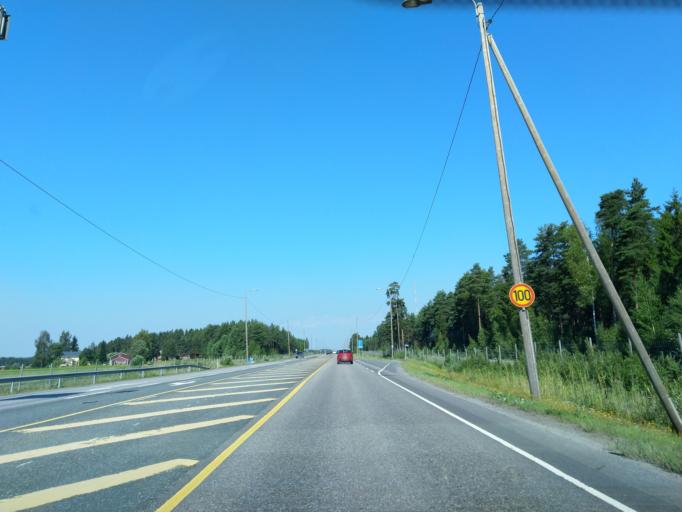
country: FI
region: Satakunta
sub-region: Pori
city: Nakkila
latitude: 61.3325
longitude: 22.0582
